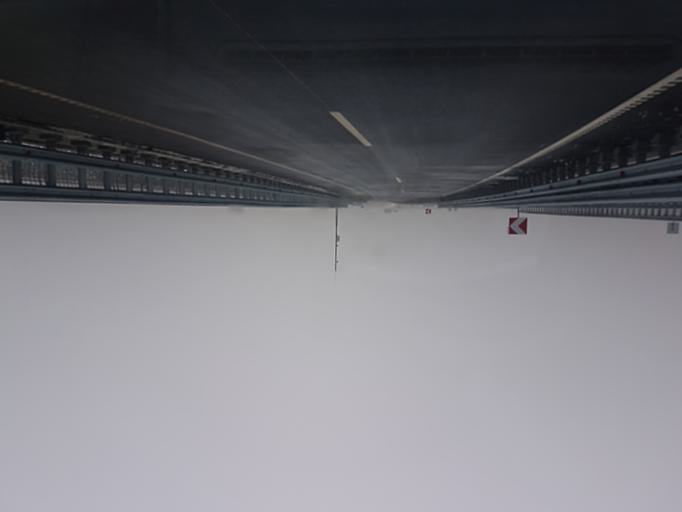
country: BY
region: Minsk
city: Samakhvalavichy
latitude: 53.7051
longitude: 27.4449
